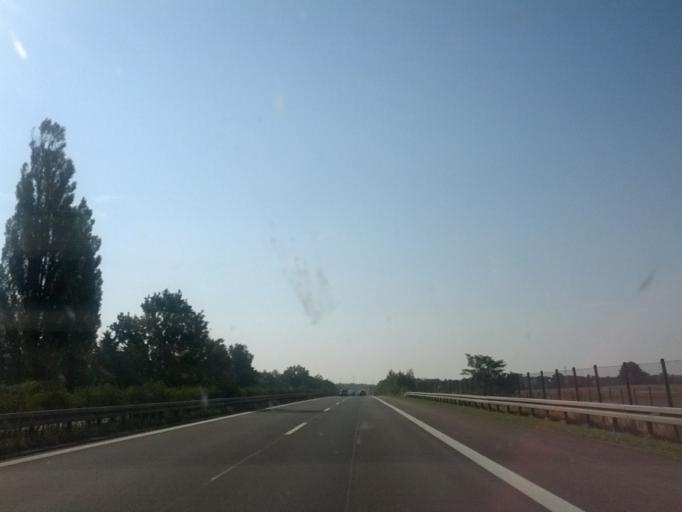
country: DE
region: Brandenburg
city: Bernau bei Berlin
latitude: 52.6796
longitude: 13.5637
